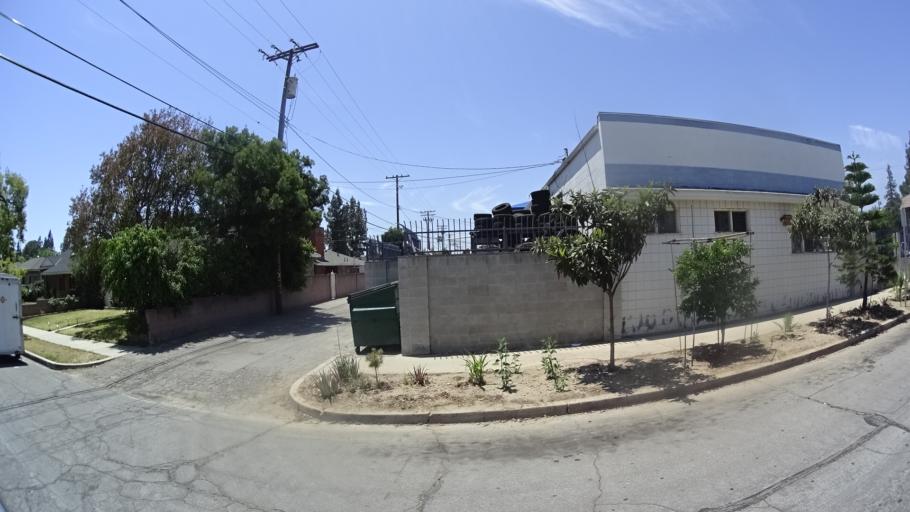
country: US
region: California
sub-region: Los Angeles County
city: Burbank
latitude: 34.1770
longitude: -118.3420
